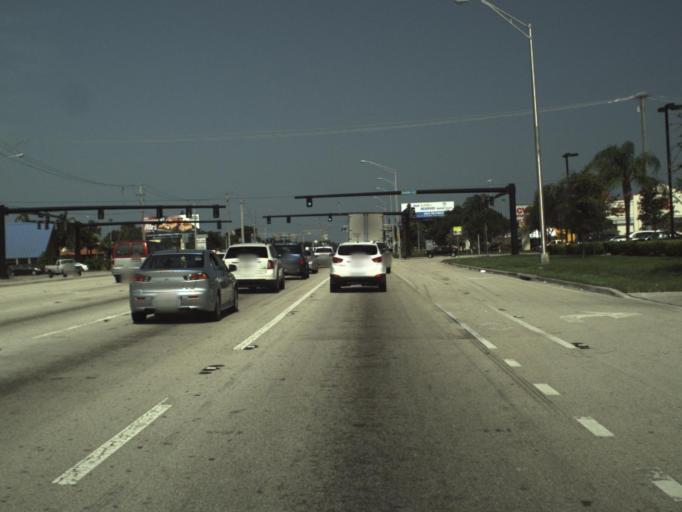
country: US
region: Florida
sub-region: Broward County
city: Tedder
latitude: 26.2747
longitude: -80.1369
